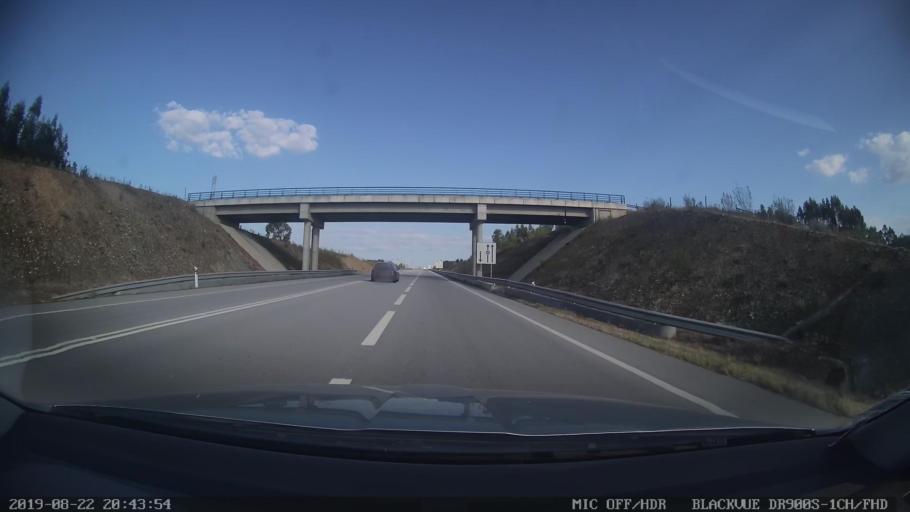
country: PT
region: Castelo Branco
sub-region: Proenca-A-Nova
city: Proenca-a-Nova
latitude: 39.7023
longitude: -7.8409
